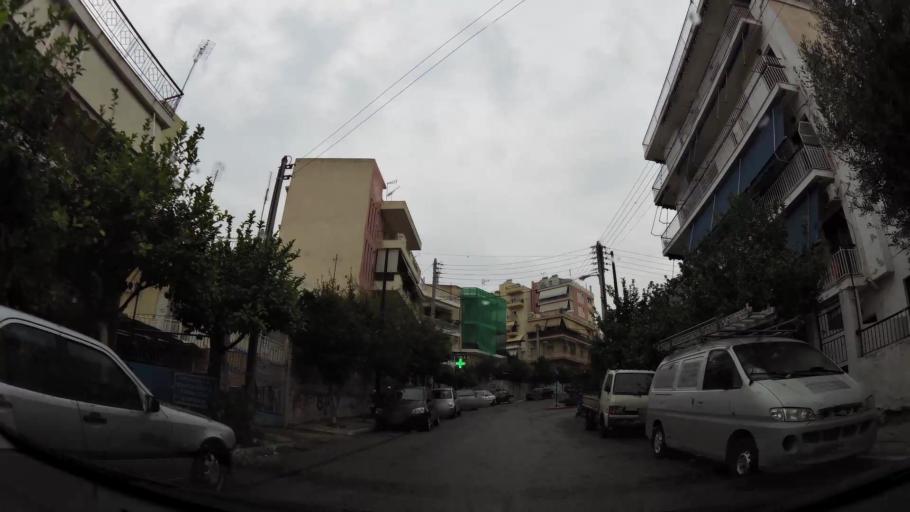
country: GR
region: Attica
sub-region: Nomarchia Athinas
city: Agia Varvara
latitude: 37.9906
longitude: 23.6527
